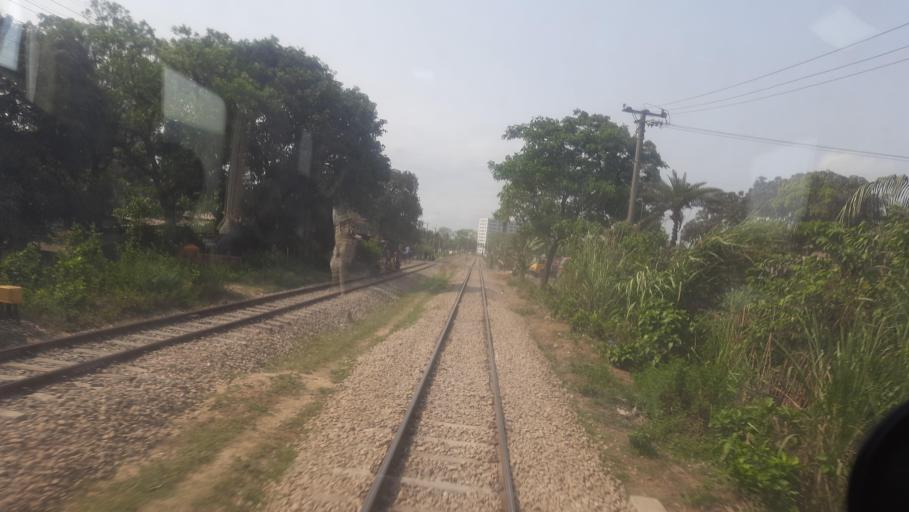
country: BD
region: Chittagong
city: Chittagong
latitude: 22.4157
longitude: 91.7543
